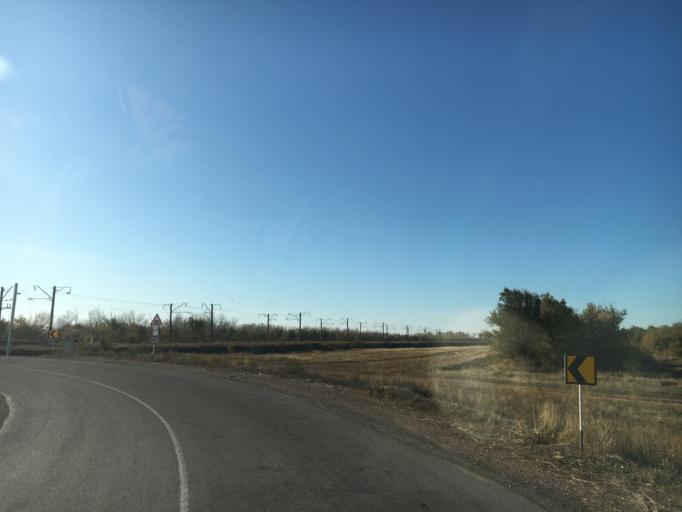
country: KZ
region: Qaraghandy
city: Tokarevka
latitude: 50.1218
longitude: 73.2148
